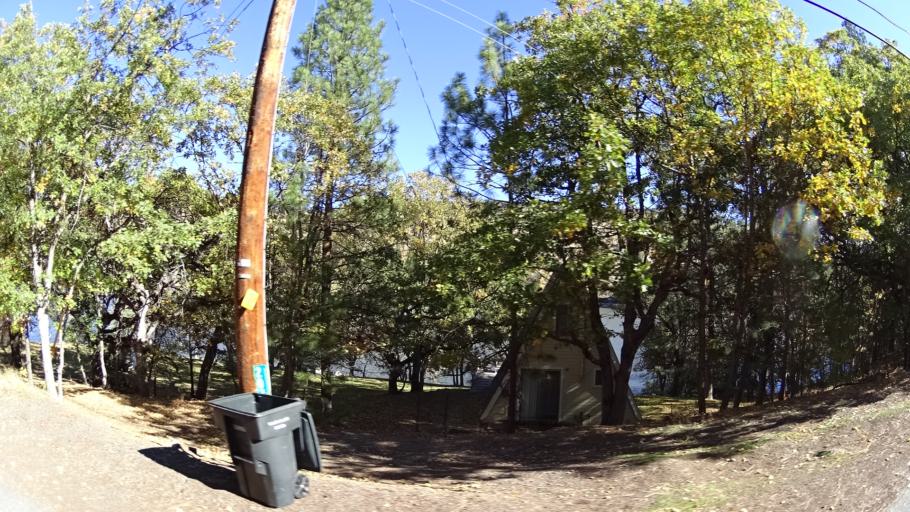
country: US
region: California
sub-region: Siskiyou County
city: Montague
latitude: 41.9673
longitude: -122.2760
